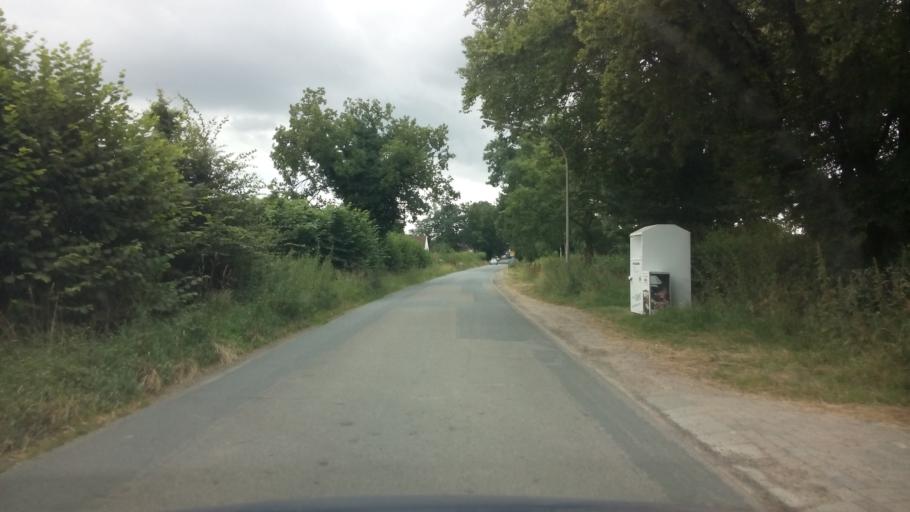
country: DE
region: Lower Saxony
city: Ritterhude
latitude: 53.2195
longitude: 8.7528
